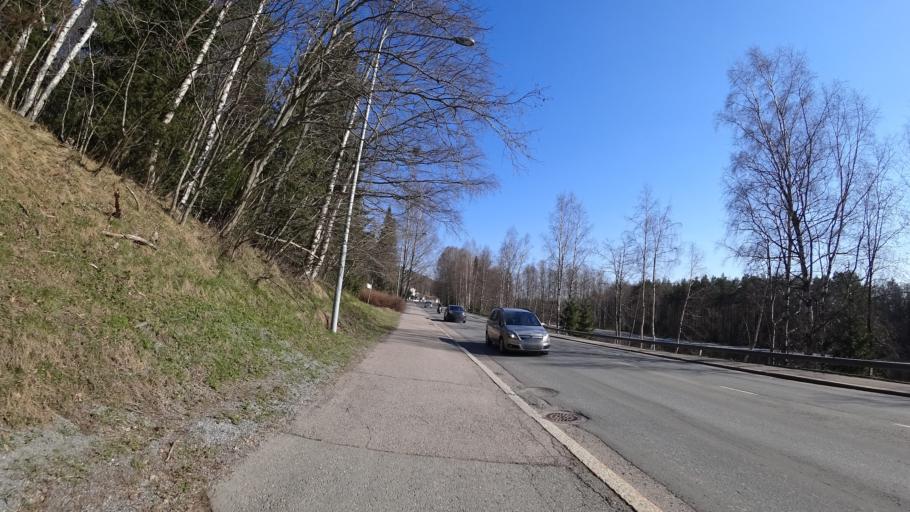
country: FI
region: Pirkanmaa
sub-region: Tampere
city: Pirkkala
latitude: 61.5186
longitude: 23.6449
